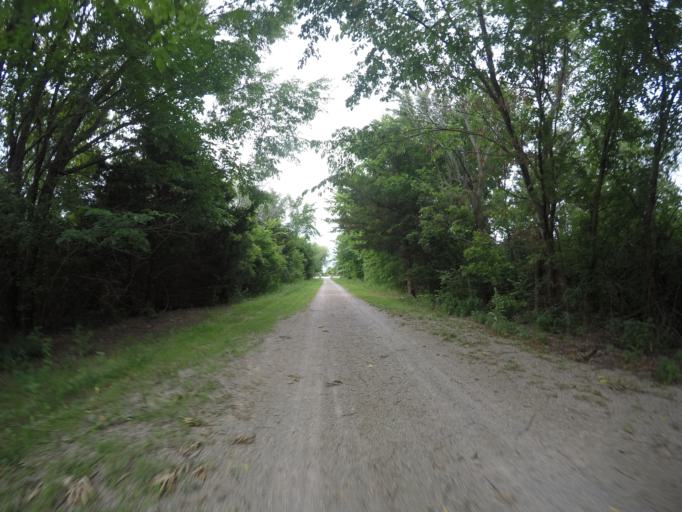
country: US
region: Kansas
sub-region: Franklin County
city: Ottawa
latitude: 38.5661
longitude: -95.2711
